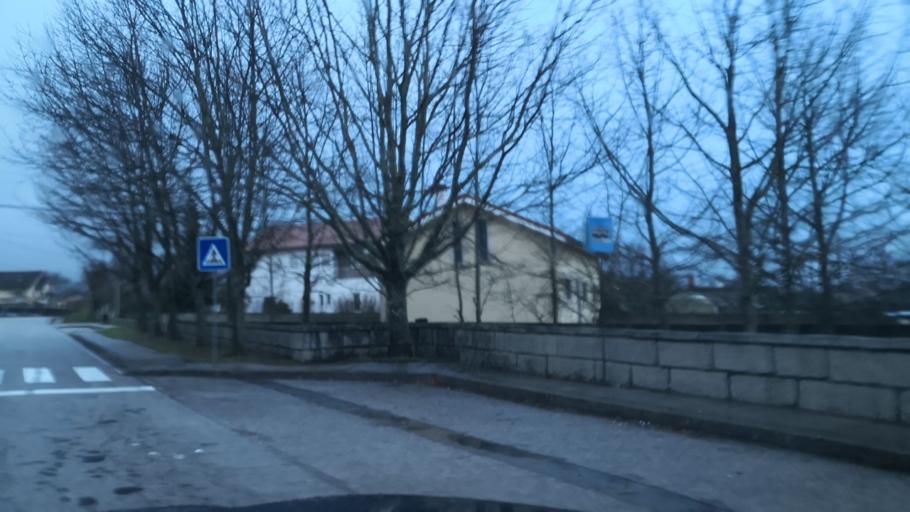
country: PT
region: Vila Real
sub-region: Vila Pouca de Aguiar
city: Vila Pouca de Aguiar
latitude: 41.4548
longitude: -7.5909
